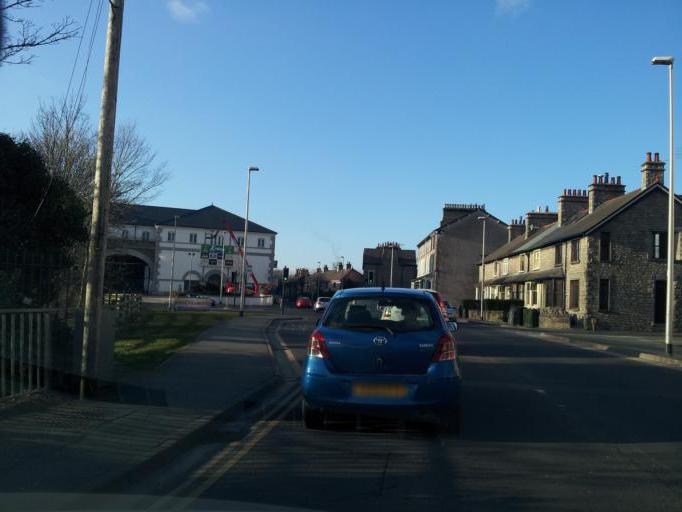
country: GB
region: England
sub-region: Cumbria
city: Kendal
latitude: 54.3184
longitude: -2.7417
